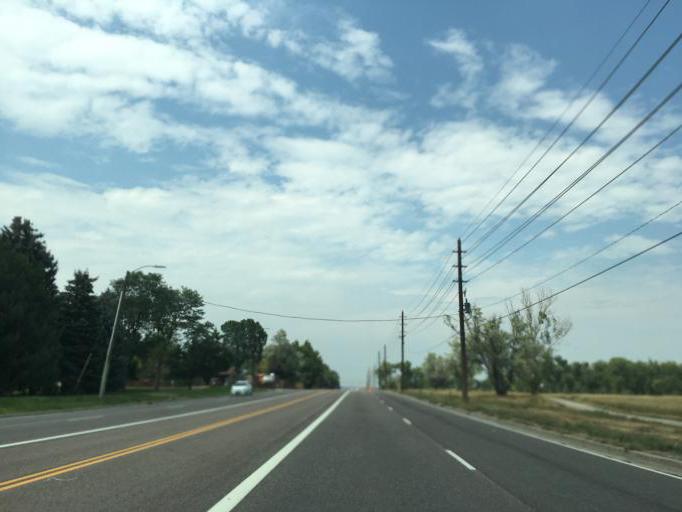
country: US
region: Colorado
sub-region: Jefferson County
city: Wheat Ridge
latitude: 39.7572
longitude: -105.1096
